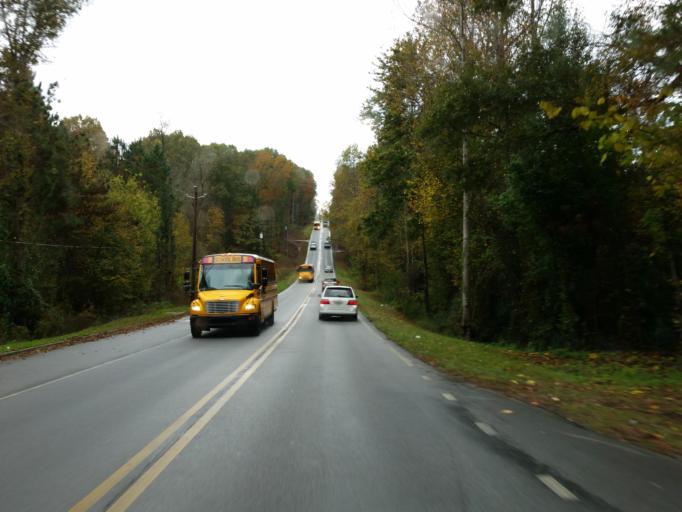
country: US
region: Georgia
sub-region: Henry County
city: Stockbridge
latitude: 33.4939
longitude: -84.2452
